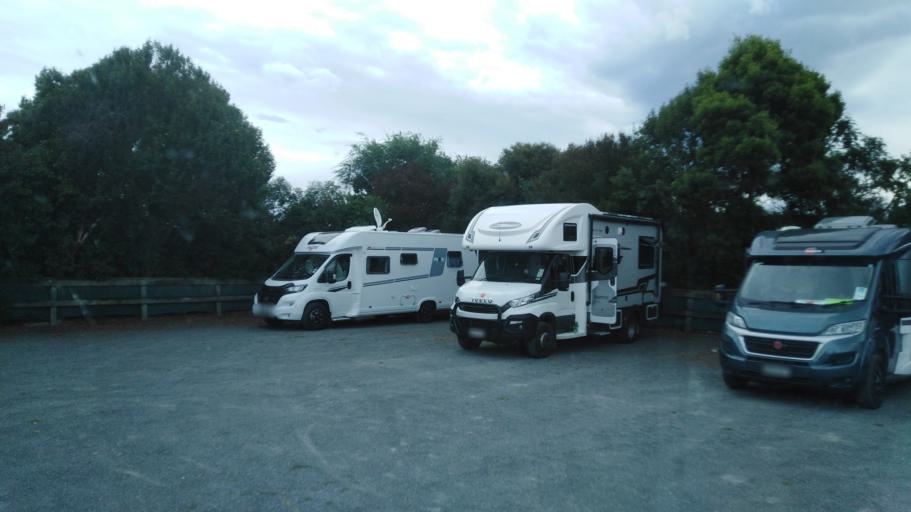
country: NZ
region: Canterbury
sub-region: Kaikoura District
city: Kaikoura
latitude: -42.3747
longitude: 173.6820
